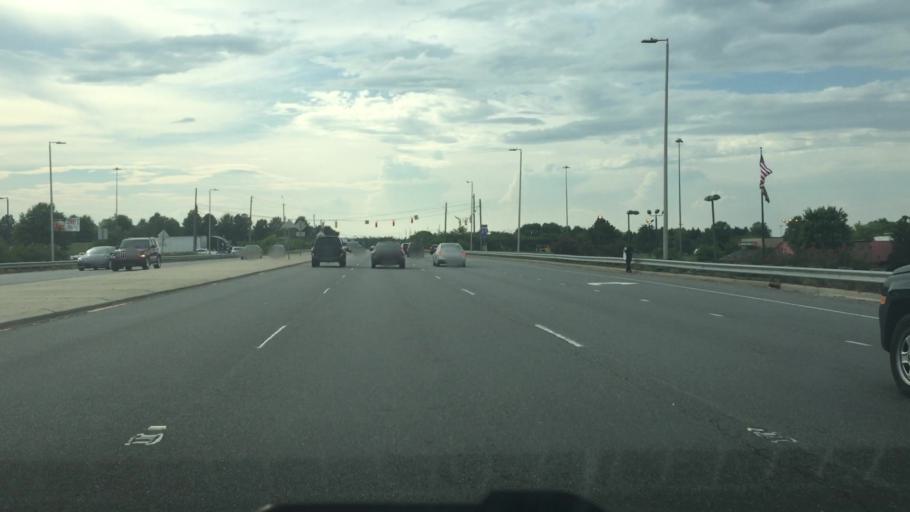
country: US
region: North Carolina
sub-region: Cabarrus County
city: Harrisburg
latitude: 35.3673
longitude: -80.7115
